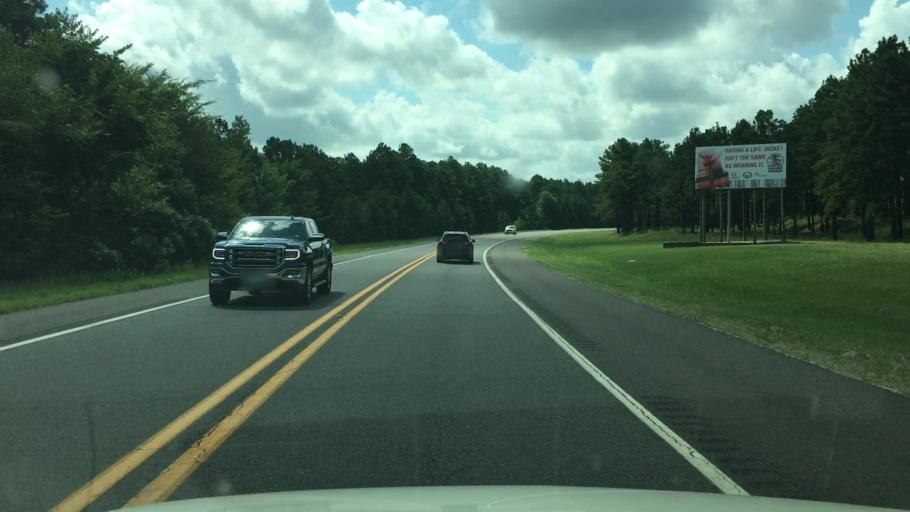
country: US
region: Arkansas
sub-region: Clark County
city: Arkadelphia
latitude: 34.2273
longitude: -93.0897
